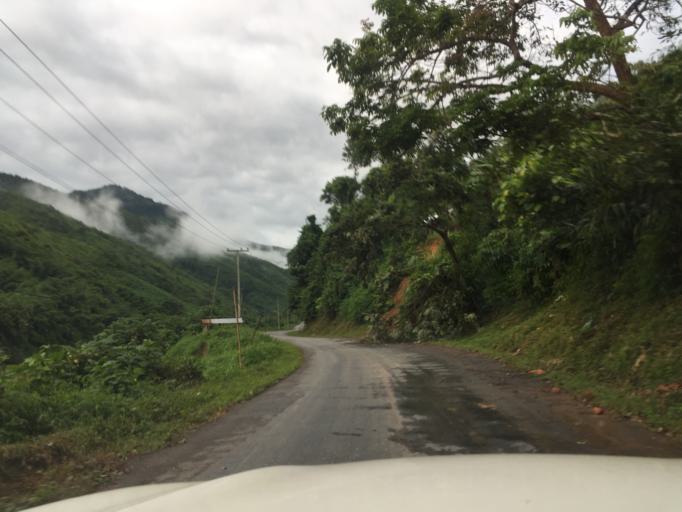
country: LA
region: Oudomxai
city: Muang La
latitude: 21.0506
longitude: 102.2410
